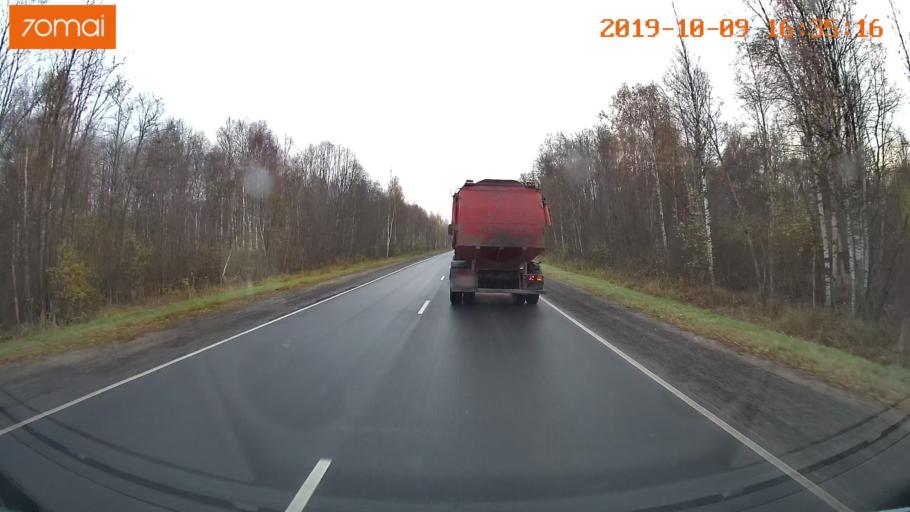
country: RU
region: Kostroma
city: Oktyabr'skiy
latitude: 57.5576
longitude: 40.9993
